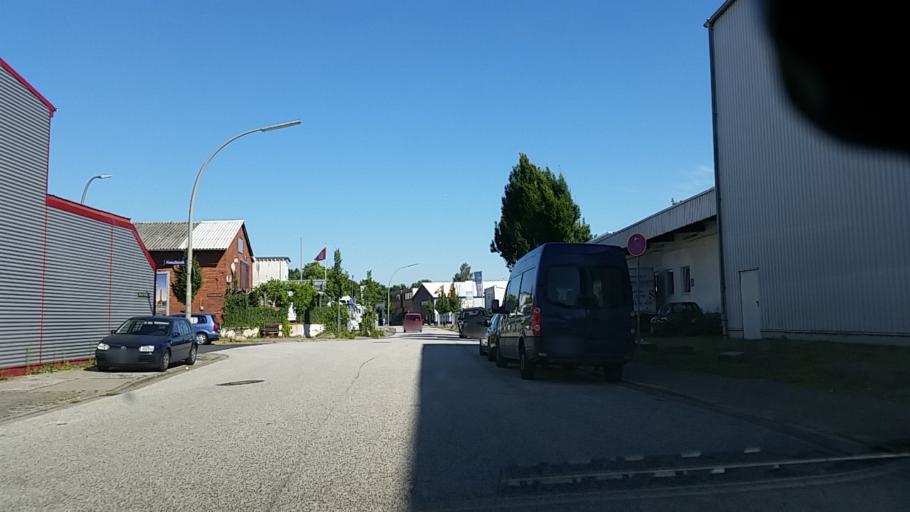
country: DE
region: Hamburg
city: Rothenburgsort
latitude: 53.5460
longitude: 10.0470
